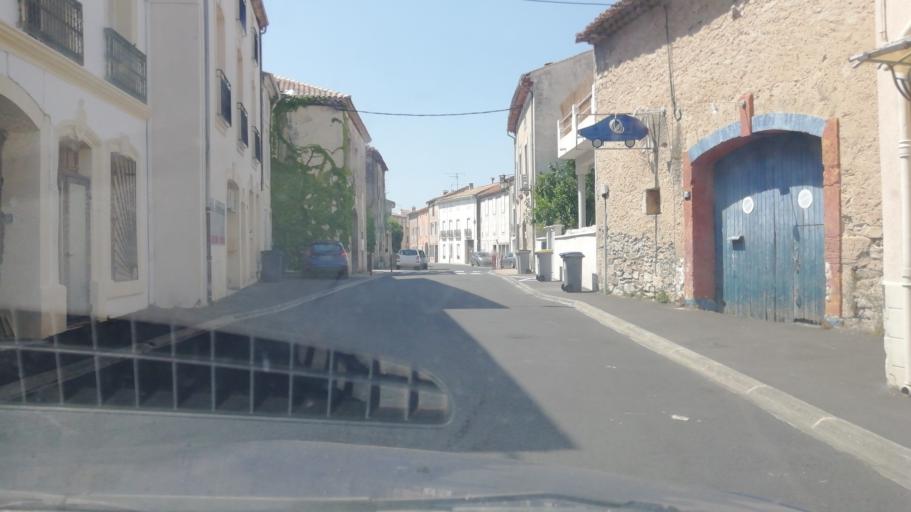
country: FR
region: Languedoc-Roussillon
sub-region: Departement de l'Herault
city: Maureilhan
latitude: 43.3578
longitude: 3.1232
